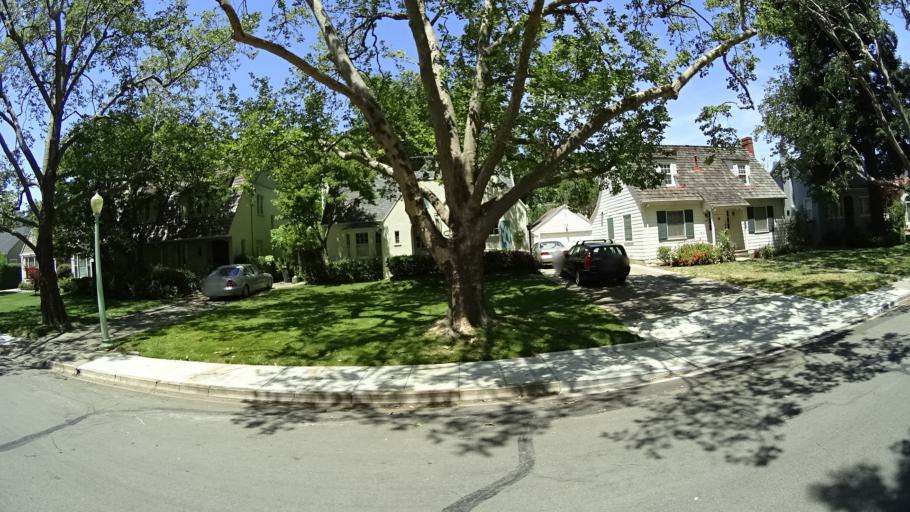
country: US
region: California
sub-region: Sacramento County
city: Sacramento
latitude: 38.5653
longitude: -121.4460
